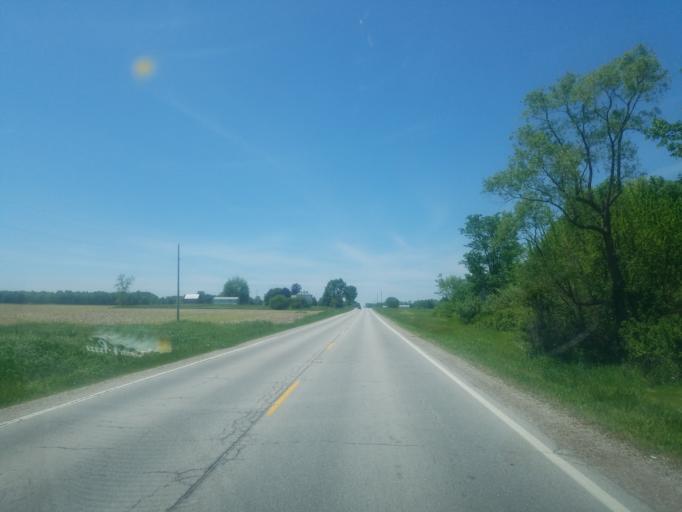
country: US
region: Ohio
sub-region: Huron County
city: New London
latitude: 41.0292
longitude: -82.4385
